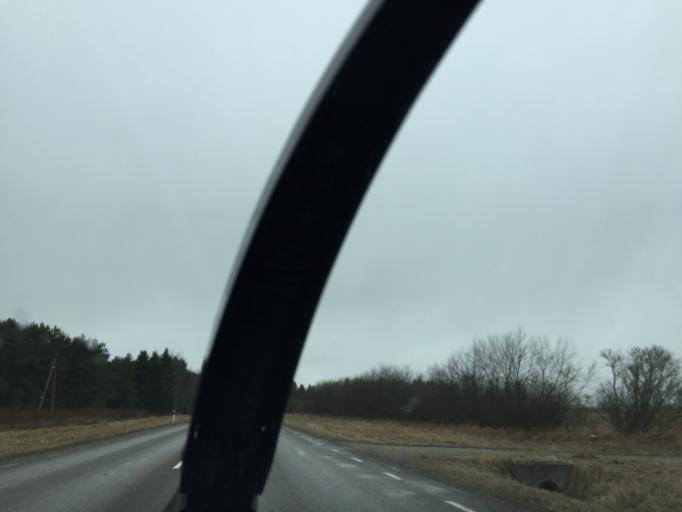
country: EE
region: Laeaene
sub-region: Ridala Parish
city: Uuemoisa
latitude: 58.8711
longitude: 23.6175
